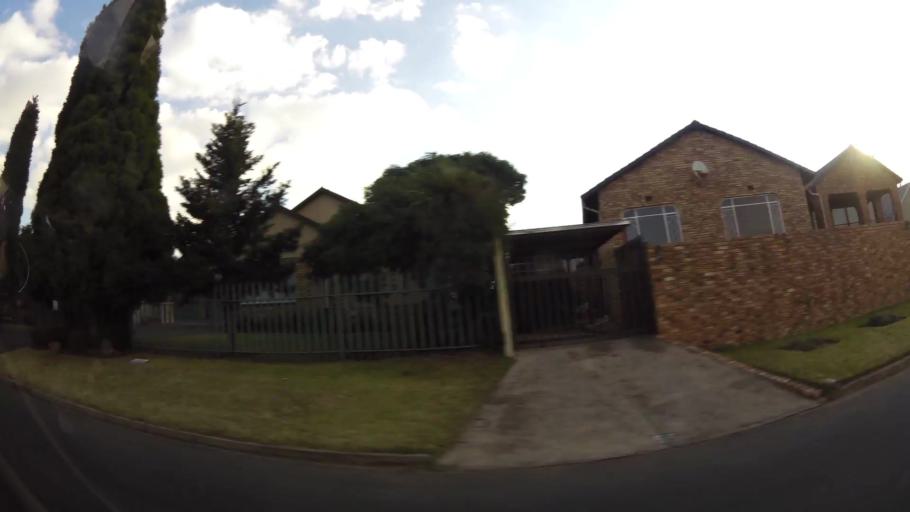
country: ZA
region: Gauteng
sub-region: West Rand District Municipality
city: Krugersdorp
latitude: -26.0741
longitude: 27.7655
